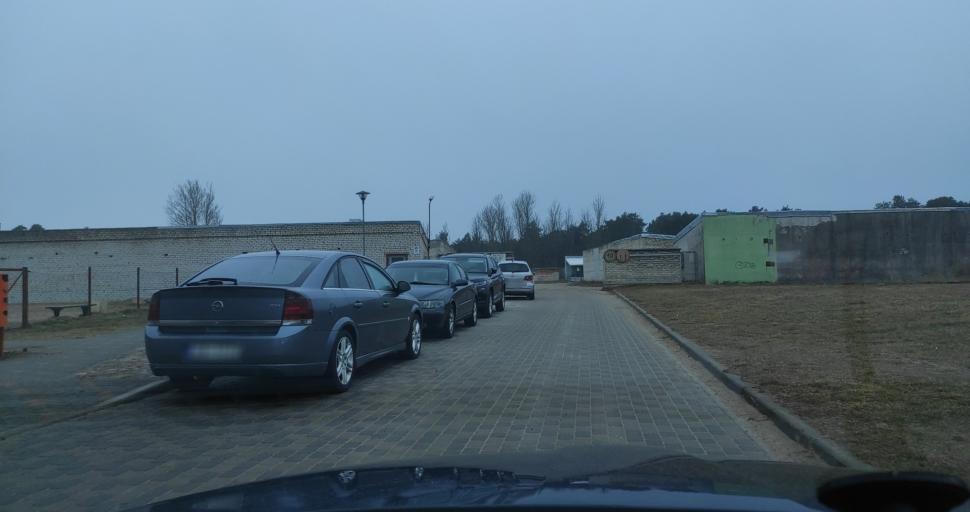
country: LV
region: Ventspils
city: Ventspils
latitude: 57.3819
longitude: 21.5486
